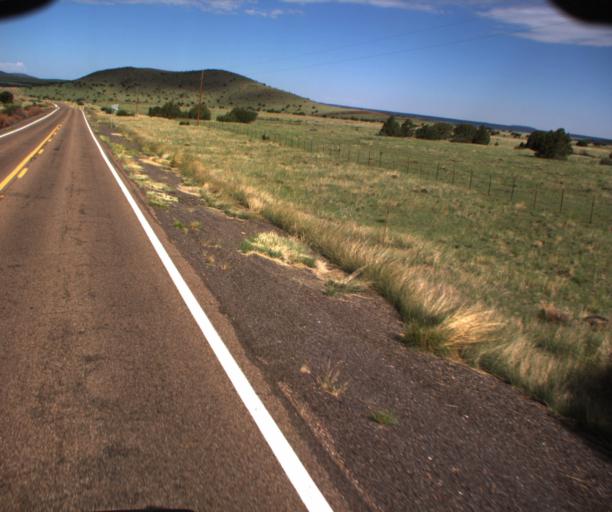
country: US
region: Arizona
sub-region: Navajo County
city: Pinetop-Lakeside
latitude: 34.2695
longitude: -109.6317
